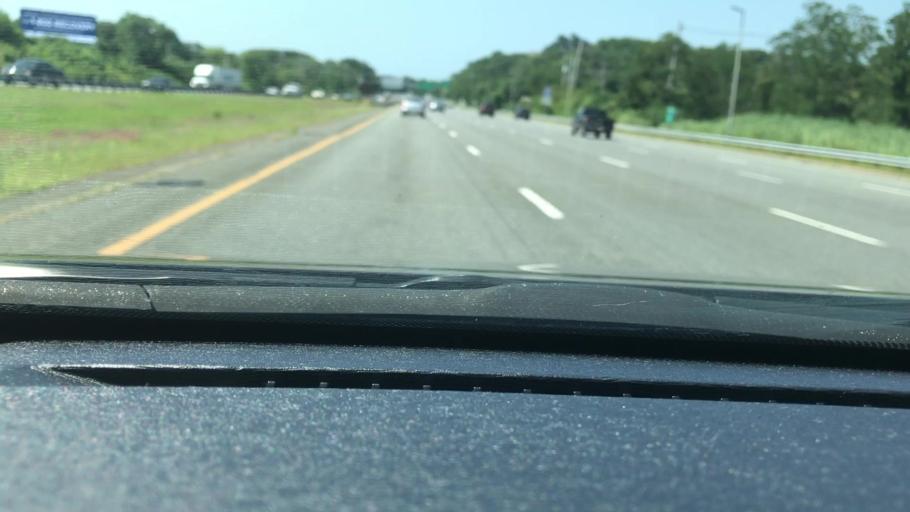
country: US
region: Massachusetts
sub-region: Essex County
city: South Peabody
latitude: 42.5235
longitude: -70.9822
